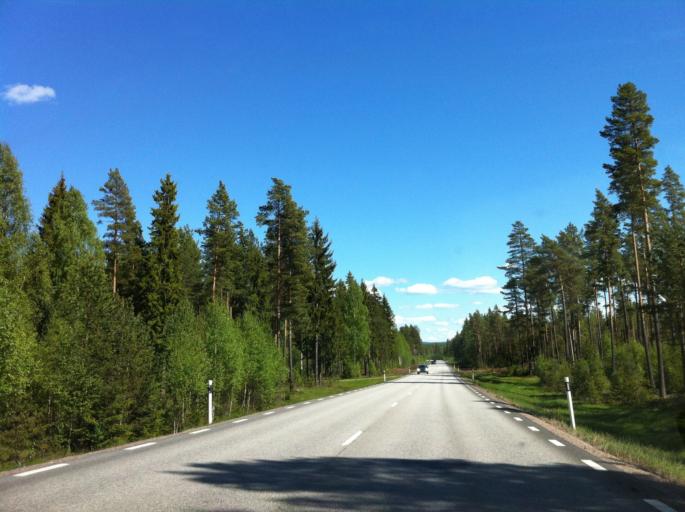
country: SE
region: Dalarna
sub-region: Leksand Municipality
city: Siljansnas
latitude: 60.9204
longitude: 14.8571
